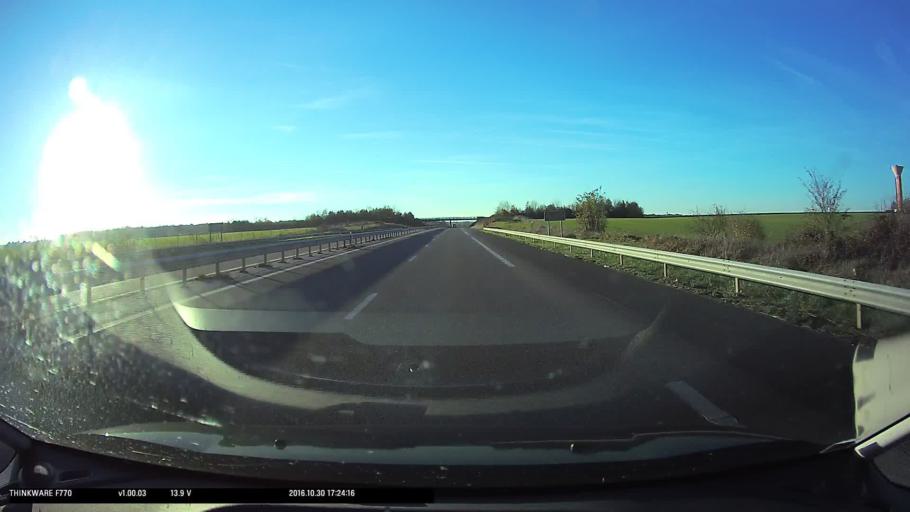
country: FR
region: Bourgogne
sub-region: Departement de la Cote-d'Or
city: Chevigny-Saint-Sauveur
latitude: 47.2683
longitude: 5.1741
